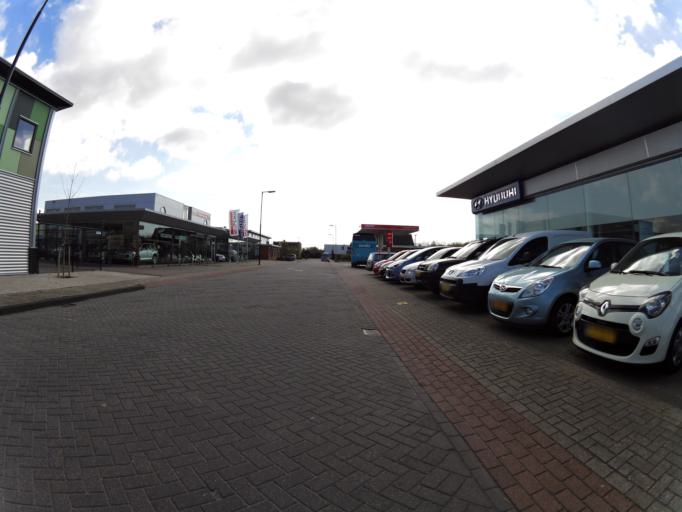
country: NL
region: South Holland
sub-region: Gemeente Brielle
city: Brielle
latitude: 51.9122
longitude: 4.1155
